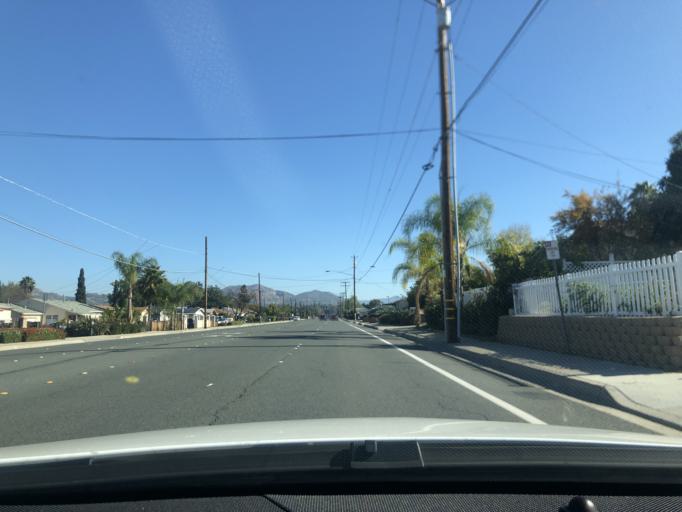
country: US
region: California
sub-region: San Diego County
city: Bostonia
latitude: 32.7876
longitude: -116.9408
